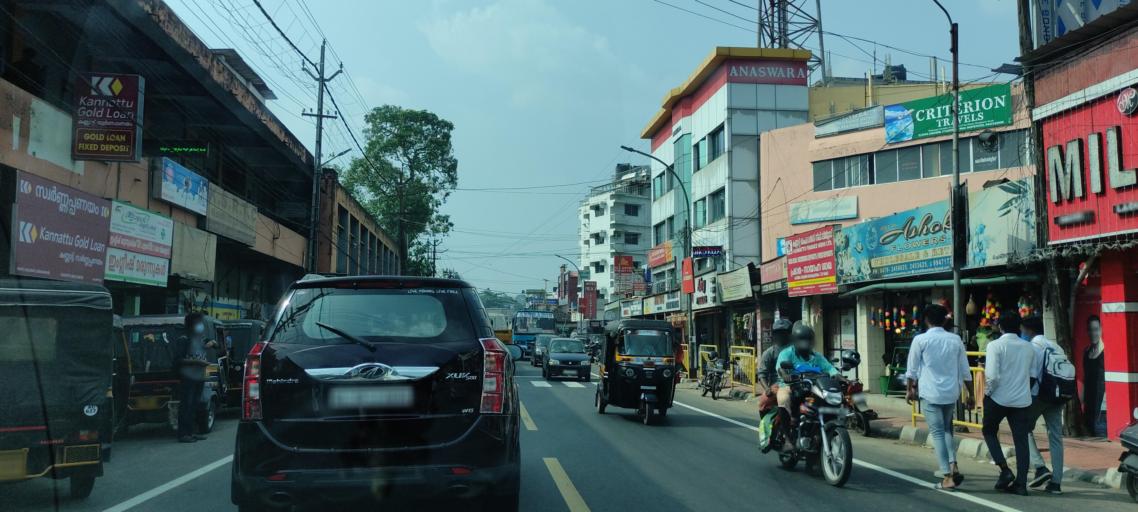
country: IN
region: Kerala
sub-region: Alappuzha
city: Chengannur
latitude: 9.3185
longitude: 76.6133
